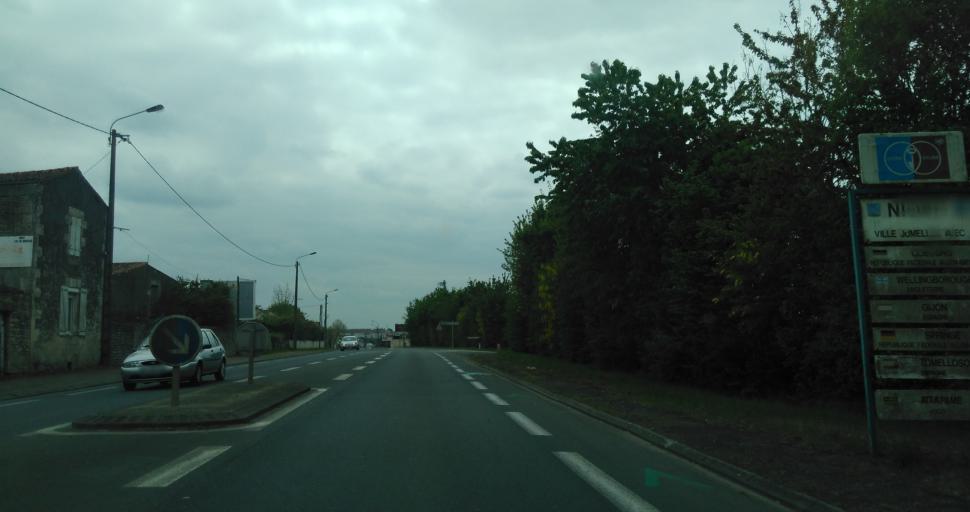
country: FR
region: Poitou-Charentes
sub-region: Departement des Deux-Sevres
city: Niort
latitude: 46.3445
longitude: -0.4441
